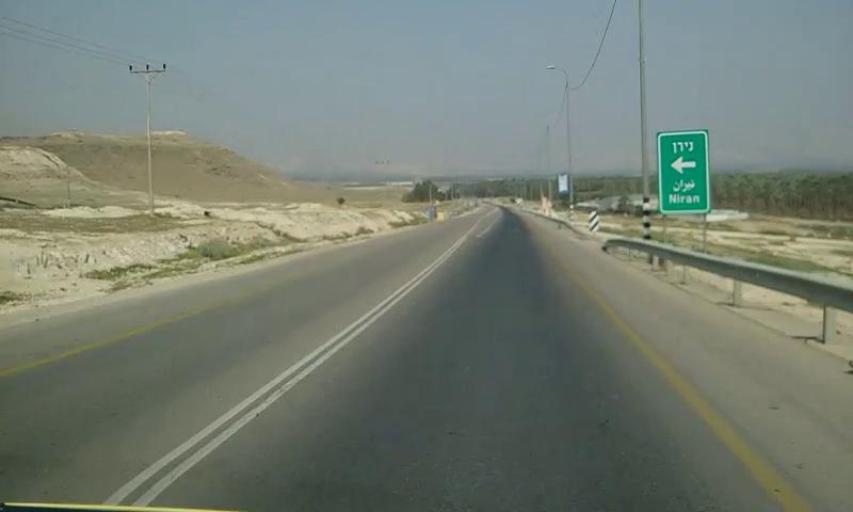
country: PS
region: West Bank
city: Al `Awja
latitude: 31.9735
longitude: 35.4696
